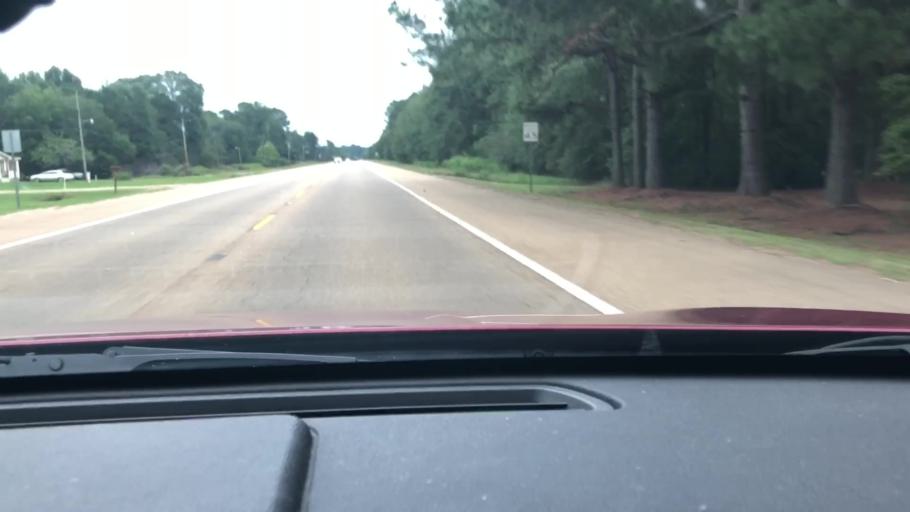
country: US
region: Arkansas
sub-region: Lafayette County
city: Stamps
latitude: 33.3590
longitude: -93.4277
